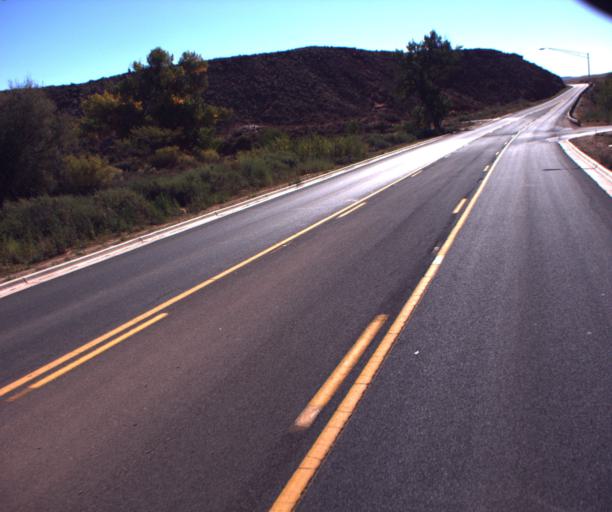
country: US
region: Arizona
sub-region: Coconino County
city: Tuba City
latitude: 36.1119
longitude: -111.2199
